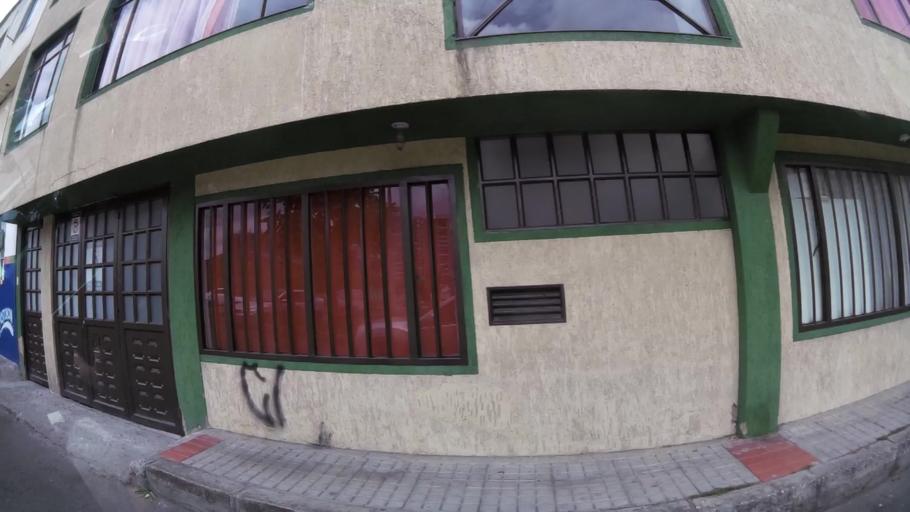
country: CO
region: Bogota D.C.
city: Bogota
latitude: 4.6405
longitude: -74.1480
